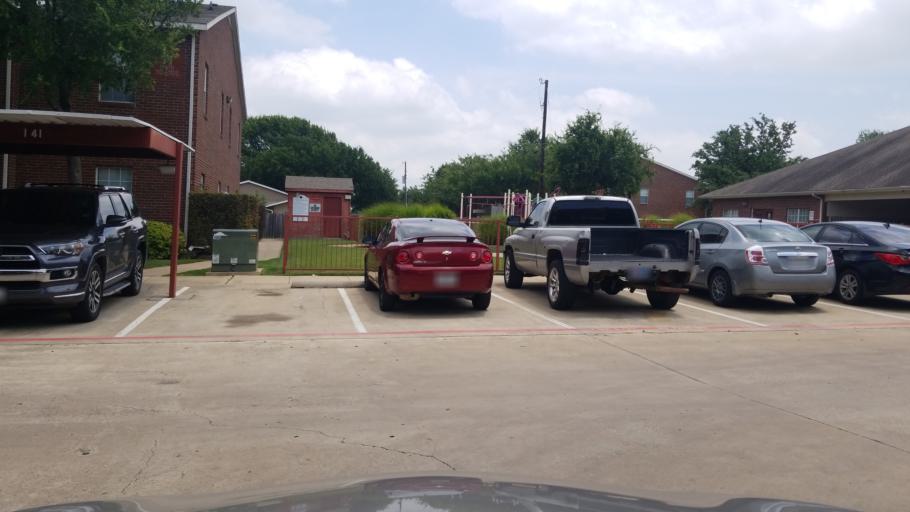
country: US
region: Texas
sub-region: Dallas County
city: Duncanville
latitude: 32.6864
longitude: -96.9113
